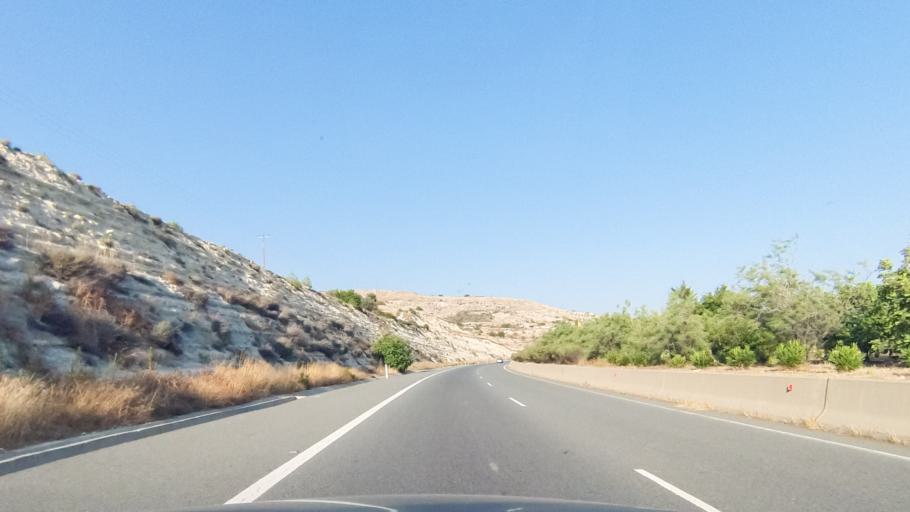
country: CY
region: Limassol
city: Sotira
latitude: 34.7039
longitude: 32.8505
